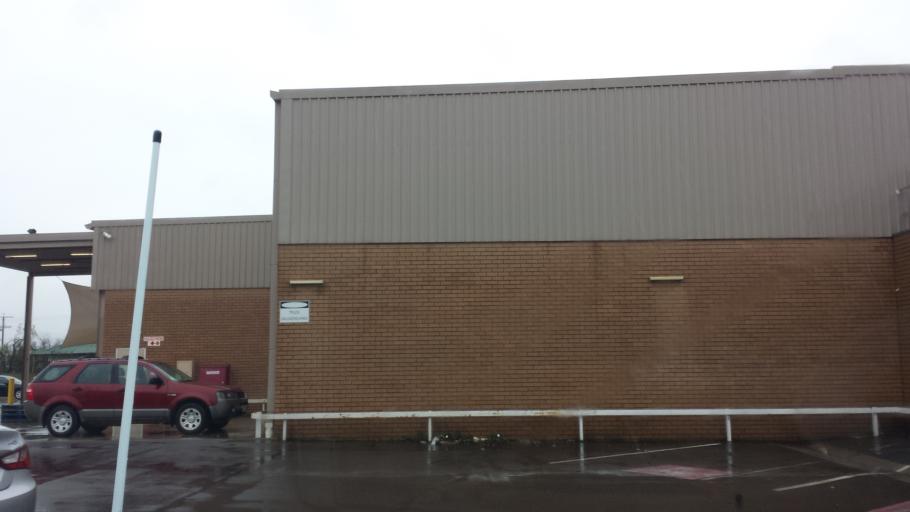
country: AU
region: Victoria
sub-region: Benalla
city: Benalla
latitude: -36.5496
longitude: 145.9856
